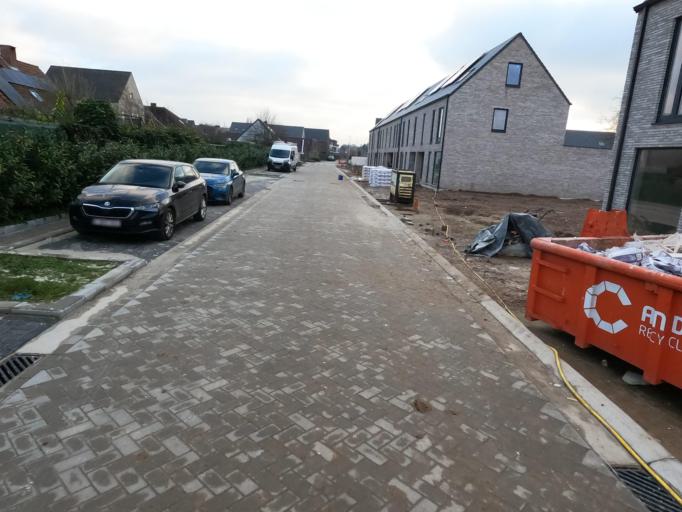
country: BE
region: Flanders
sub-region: Provincie Antwerpen
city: Boechout
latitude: 51.1714
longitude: 4.5027
